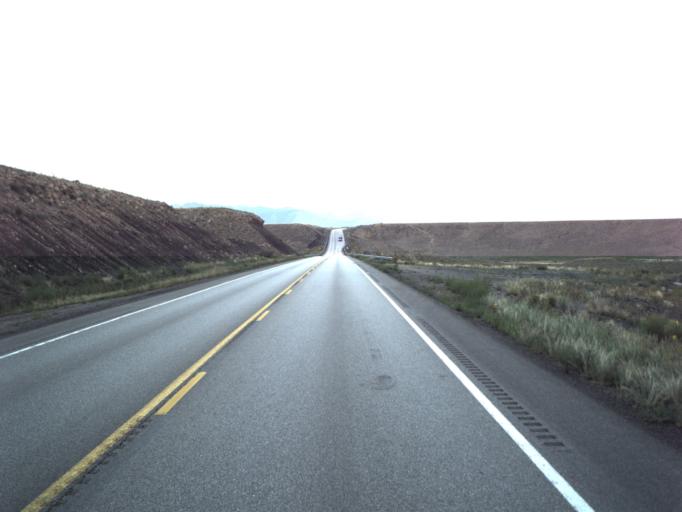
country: US
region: Utah
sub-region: Carbon County
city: East Carbon City
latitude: 39.5166
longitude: -110.5521
